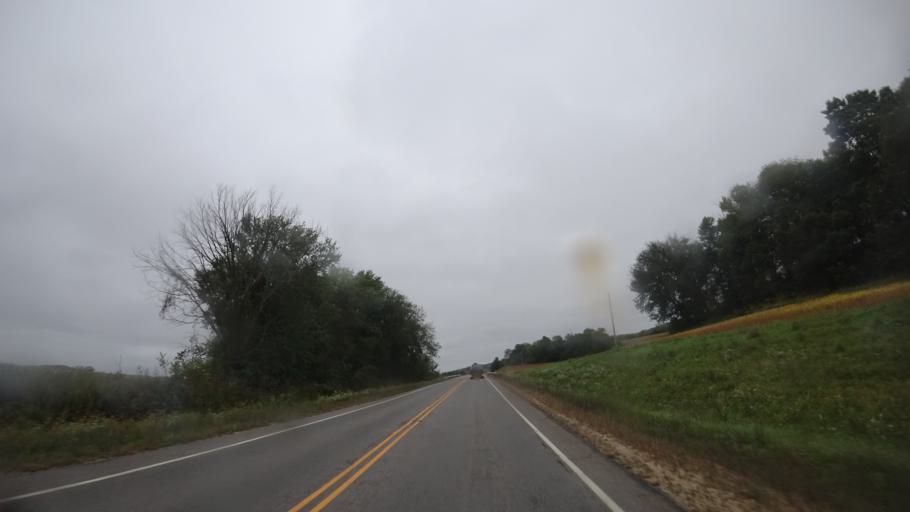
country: US
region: Wisconsin
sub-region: Crawford County
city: Prairie du Chien
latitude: 43.0318
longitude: -90.9930
